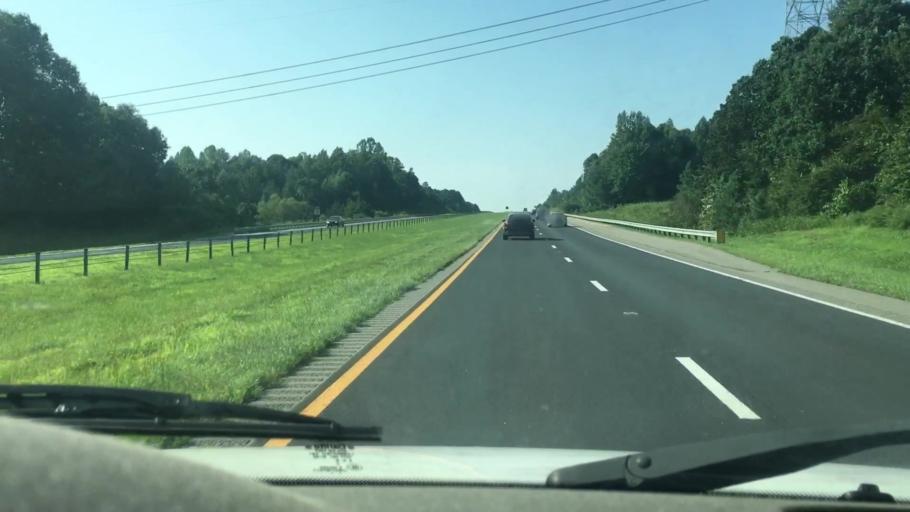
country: US
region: North Carolina
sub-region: Lincoln County
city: Lowesville
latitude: 35.4103
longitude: -80.9985
